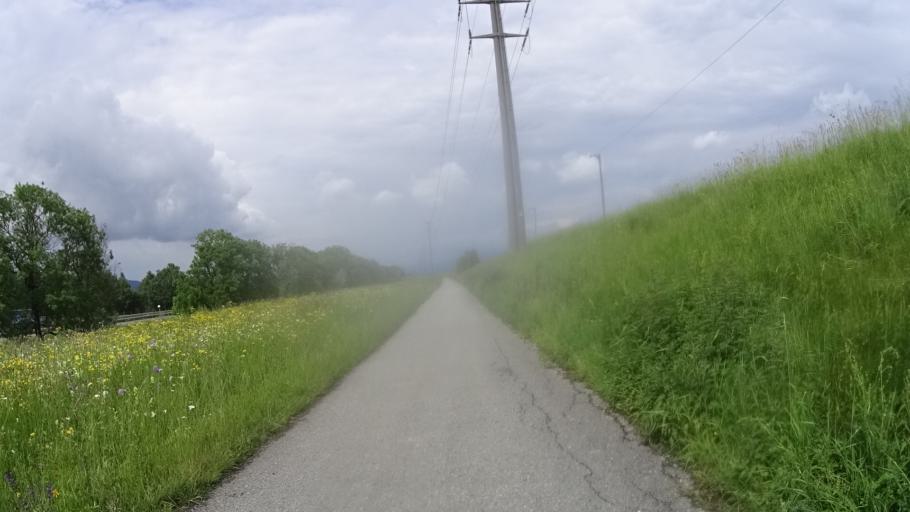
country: CH
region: Saint Gallen
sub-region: Wahlkreis Rheintal
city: Diepoldsau
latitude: 47.3762
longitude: 9.6337
